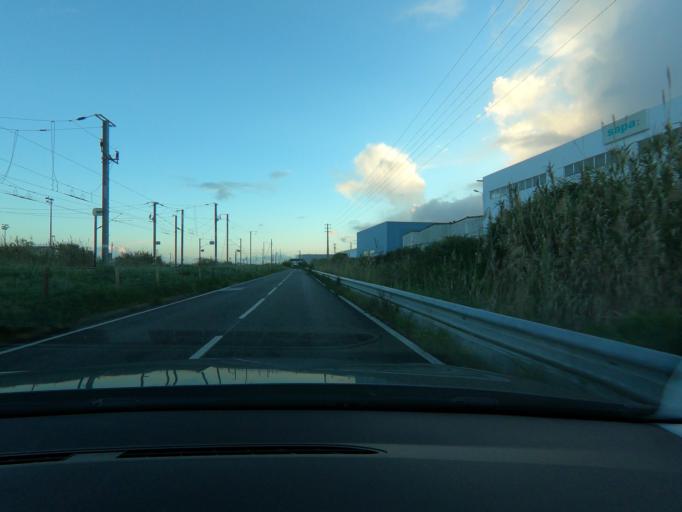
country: PT
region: Lisbon
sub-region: Vila Franca de Xira
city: Castanheira do Ribatejo
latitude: 38.9774
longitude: -8.9739
